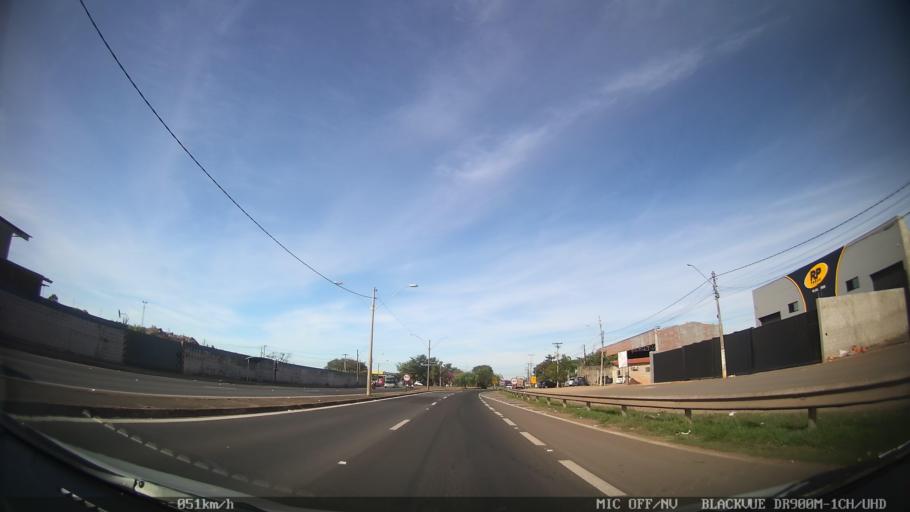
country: BR
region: Sao Paulo
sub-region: Piracicaba
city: Piracicaba
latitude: -22.7618
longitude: -47.6453
